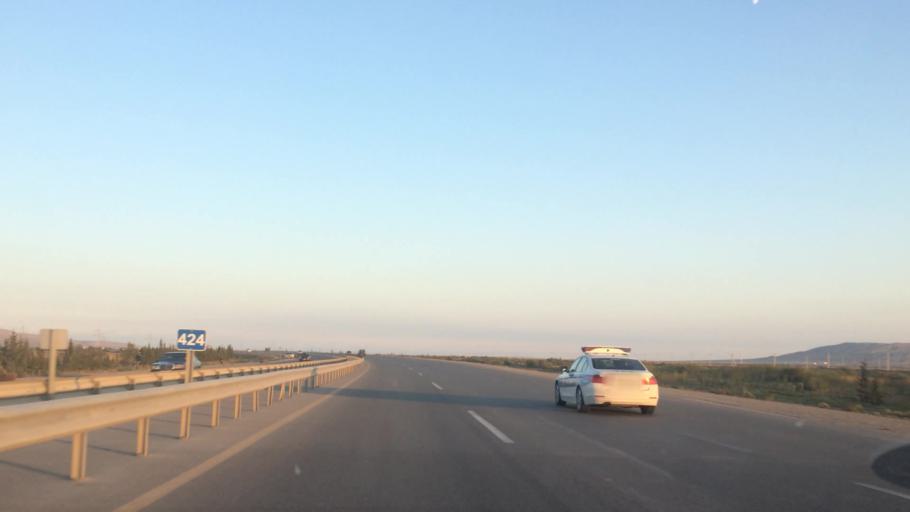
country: AZ
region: Baki
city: Qobustan
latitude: 39.9842
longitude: 49.2128
